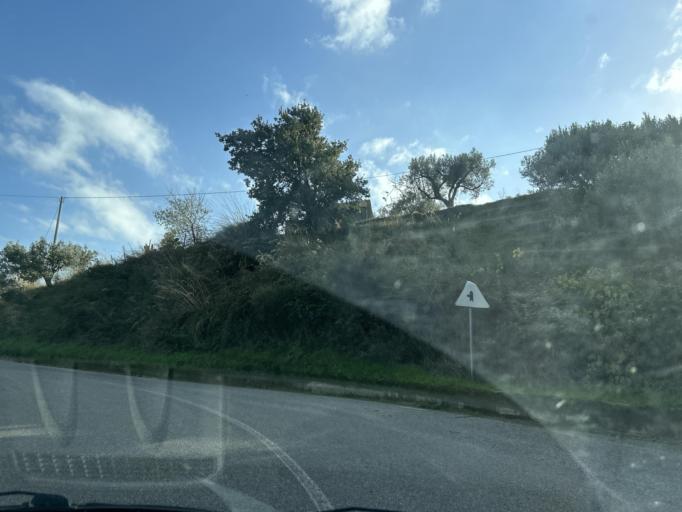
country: IT
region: Calabria
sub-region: Provincia di Catanzaro
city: Montepaone
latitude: 38.7204
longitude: 16.5040
